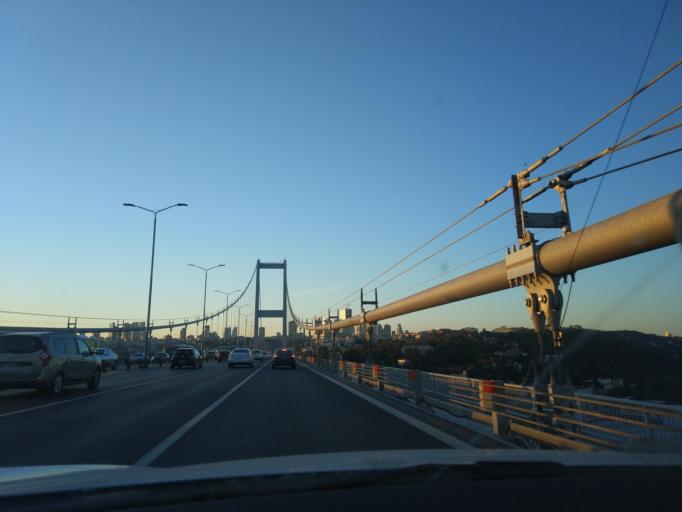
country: TR
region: Istanbul
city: UEskuedar
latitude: 41.0456
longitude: 29.0344
